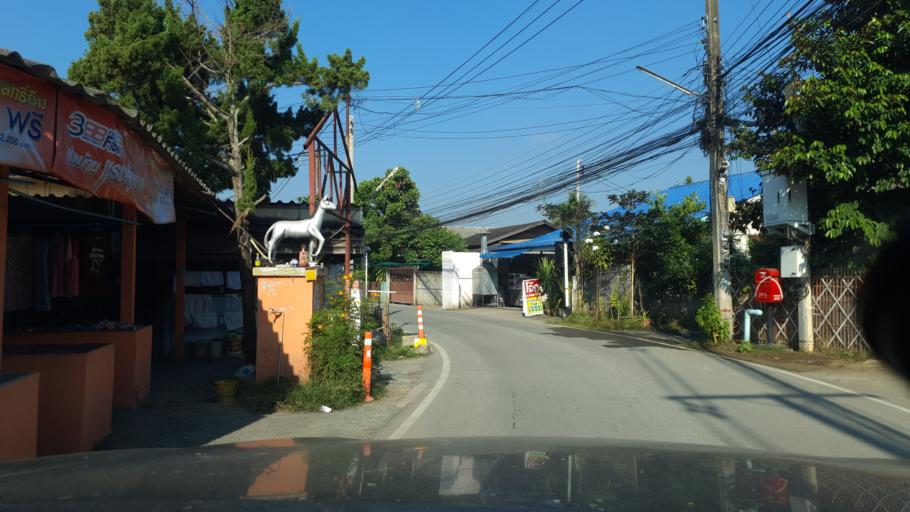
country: TH
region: Chiang Mai
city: San Kamphaeng
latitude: 18.7562
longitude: 99.1587
